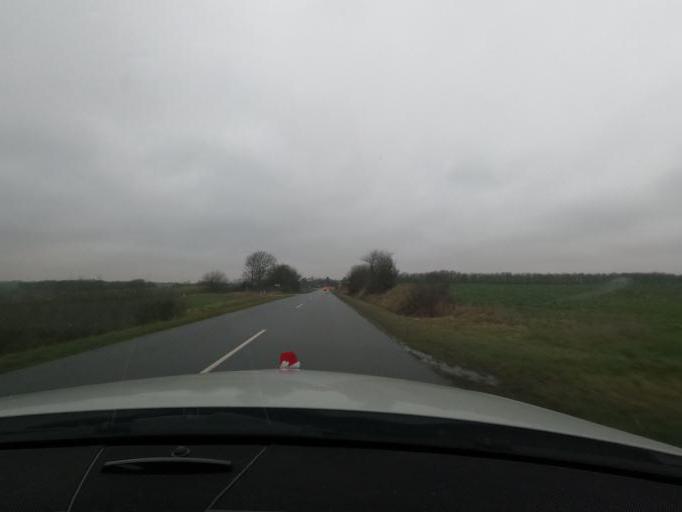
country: DK
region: South Denmark
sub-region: Haderslev Kommune
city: Haderslev
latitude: 55.2007
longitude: 9.4550
